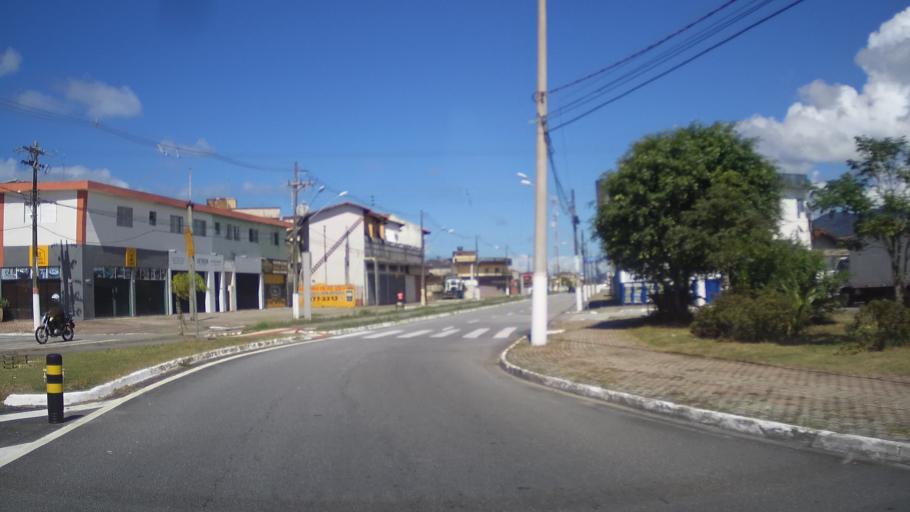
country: BR
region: Sao Paulo
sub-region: Mongagua
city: Mongagua
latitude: -24.0525
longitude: -46.5420
